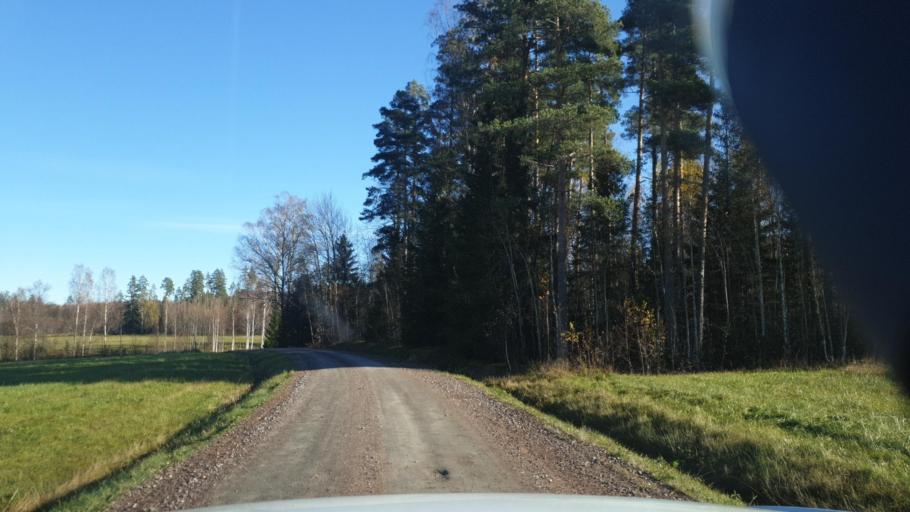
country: SE
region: Vaermland
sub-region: Karlstads Kommun
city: Edsvalla
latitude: 59.4858
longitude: 13.1556
